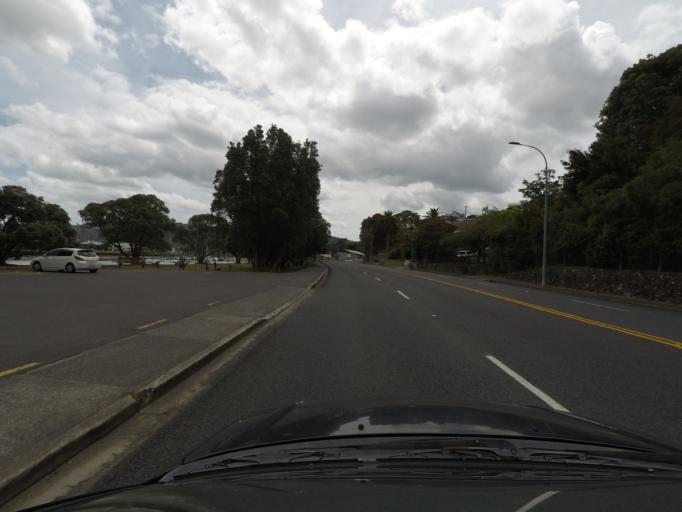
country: NZ
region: Northland
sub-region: Whangarei
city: Whangarei
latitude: -35.7270
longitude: 174.3334
